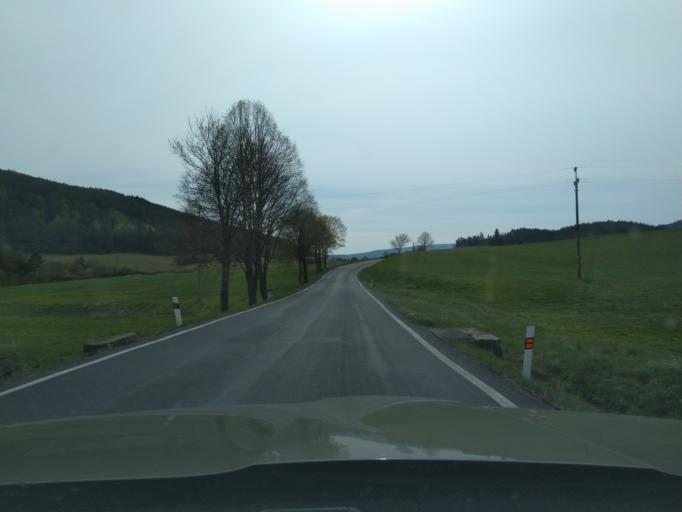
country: CZ
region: Plzensky
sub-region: Okres Klatovy
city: Susice
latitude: 49.2351
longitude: 13.5782
